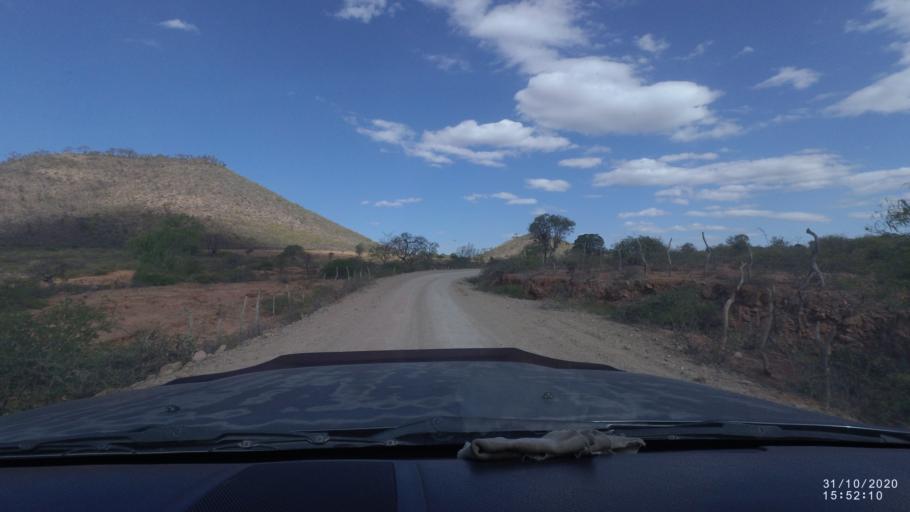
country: BO
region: Chuquisaca
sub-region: Provincia Zudanez
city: Mojocoya
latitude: -18.3178
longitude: -64.6957
